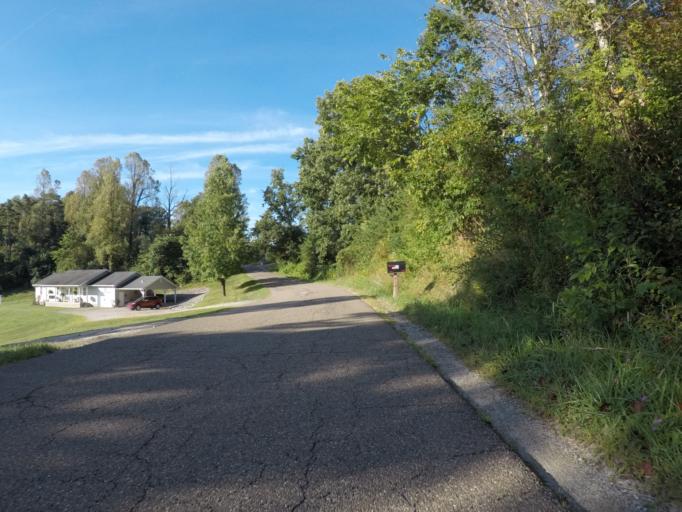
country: US
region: Ohio
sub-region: Lawrence County
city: Coal Grove
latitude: 38.5951
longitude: -82.5468
